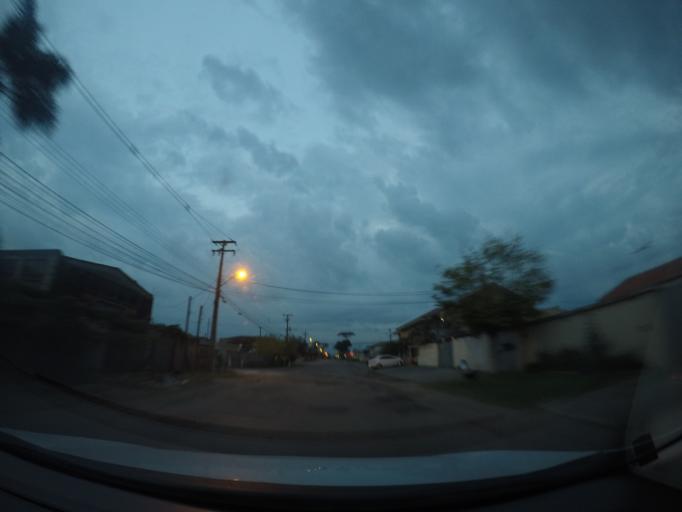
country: BR
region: Parana
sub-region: Sao Jose Dos Pinhais
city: Sao Jose dos Pinhais
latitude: -25.5043
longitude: -49.2307
